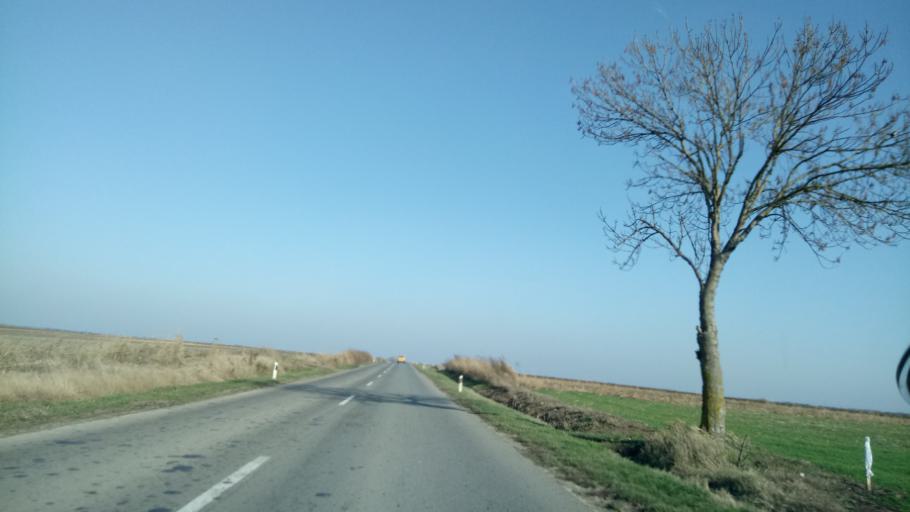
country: RS
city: Putinci
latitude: 44.9989
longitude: 19.9960
